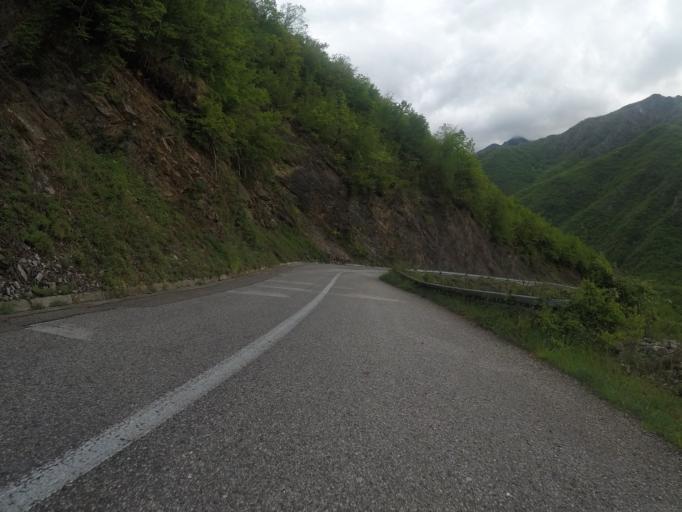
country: BA
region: Federation of Bosnia and Herzegovina
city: Siroki Brijeg
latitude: 43.5408
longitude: 17.5925
